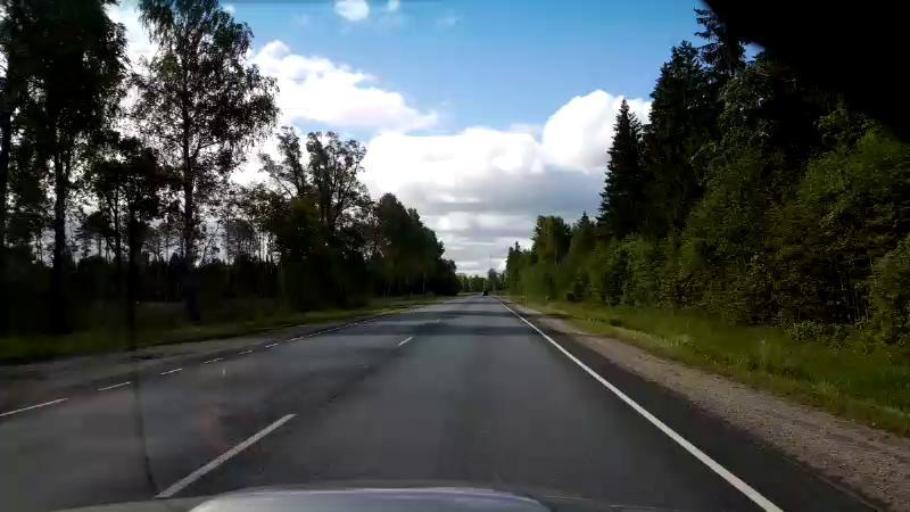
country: EE
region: Raplamaa
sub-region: Maerjamaa vald
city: Marjamaa
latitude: 59.0341
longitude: 24.4441
